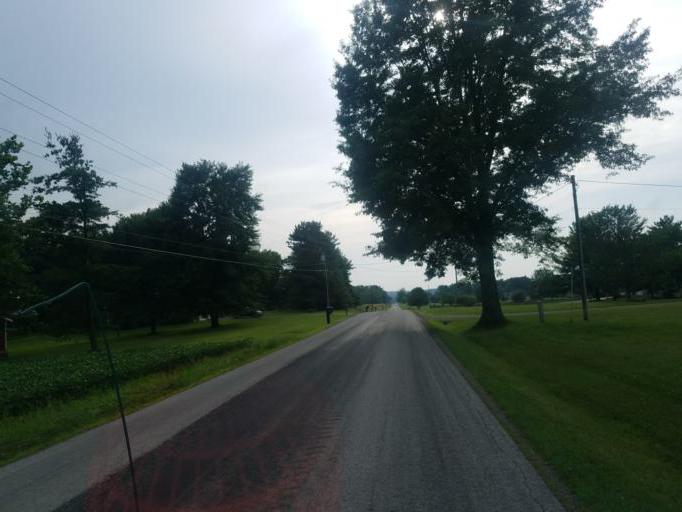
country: US
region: Ohio
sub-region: Wayne County
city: West Salem
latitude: 40.9009
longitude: -82.1014
